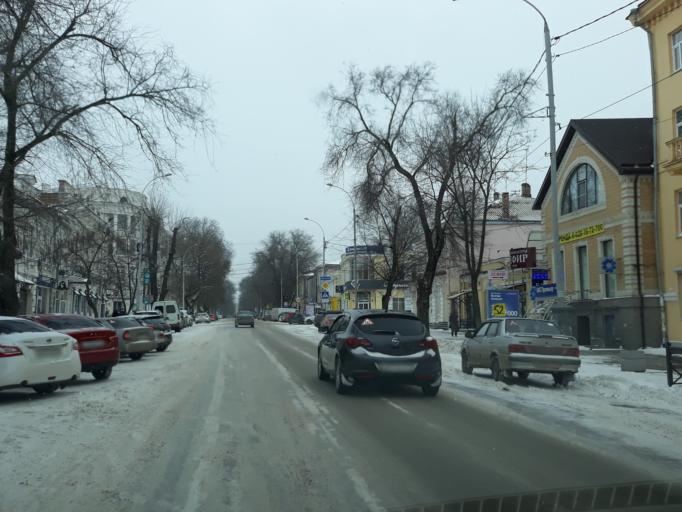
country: RU
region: Rostov
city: Taganrog
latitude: 47.2152
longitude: 38.9295
